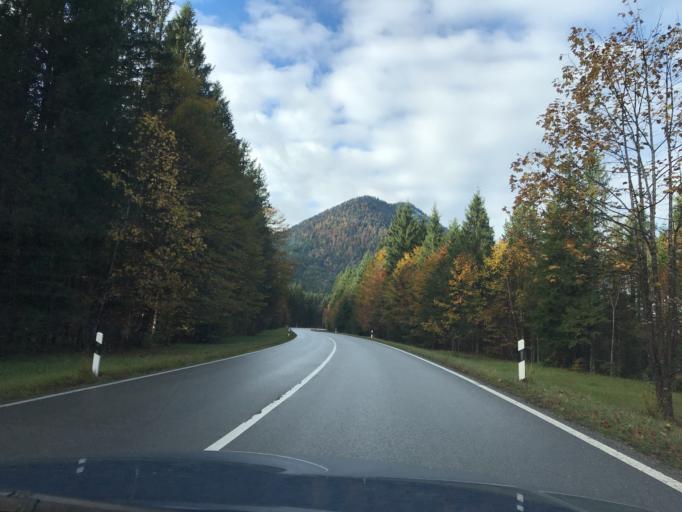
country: DE
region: Bavaria
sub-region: Upper Bavaria
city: Jachenau
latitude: 47.5678
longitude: 11.5250
